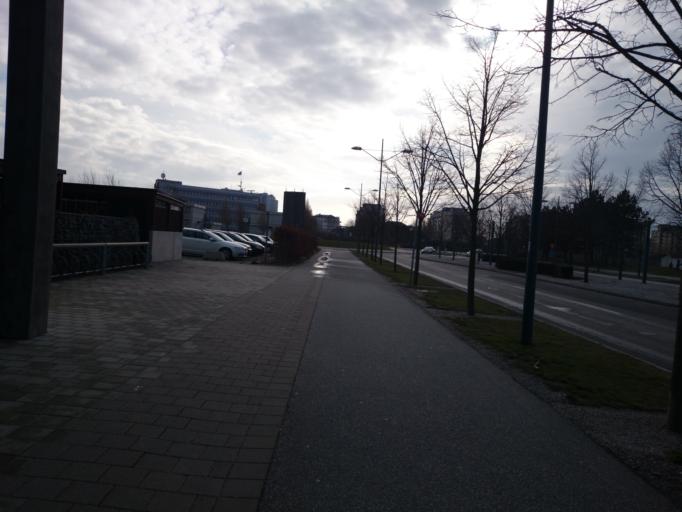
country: SE
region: Skane
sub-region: Malmo
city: Malmoe
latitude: 55.6075
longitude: 12.9790
